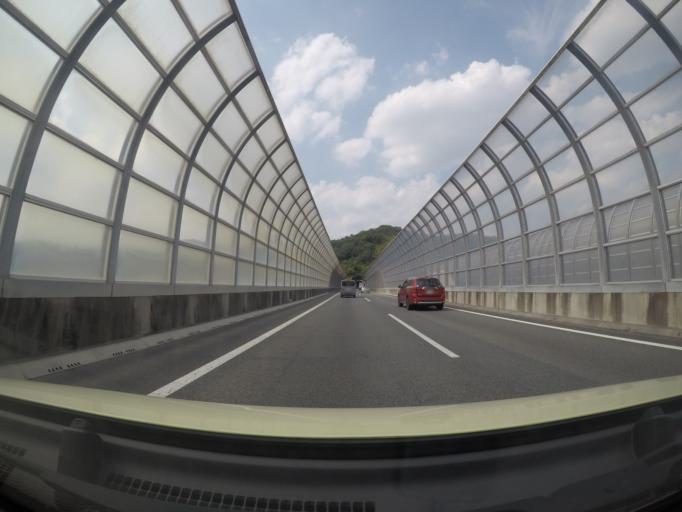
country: JP
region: Tokyo
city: Fussa
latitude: 35.7418
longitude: 139.2815
